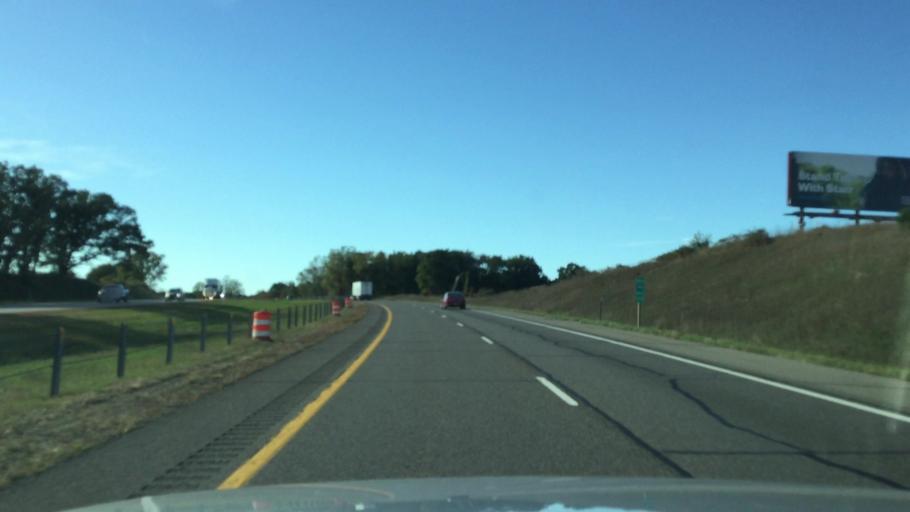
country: US
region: Michigan
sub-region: Calhoun County
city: Albion
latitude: 42.2822
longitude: -84.7923
